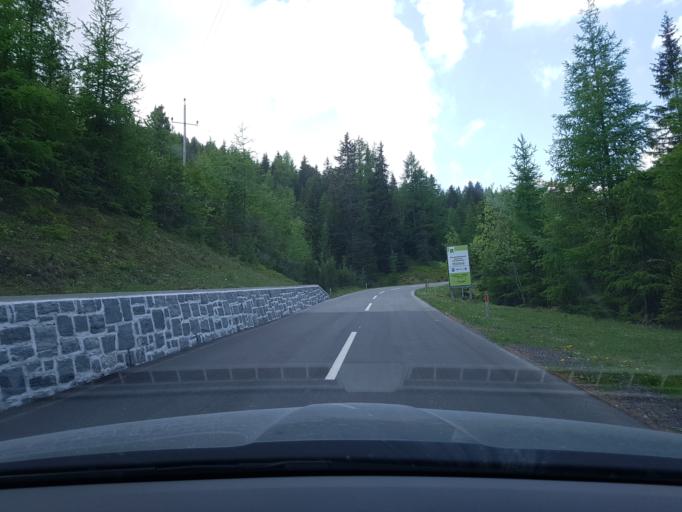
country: AT
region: Salzburg
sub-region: Politischer Bezirk Tamsweg
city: Thomatal
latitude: 46.9549
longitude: 13.7291
